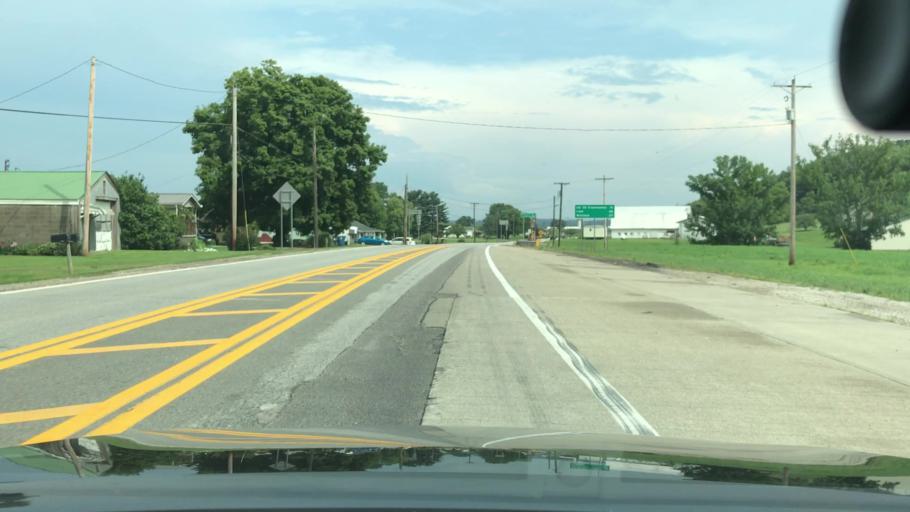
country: US
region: West Virginia
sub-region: Putnam County
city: Buffalo
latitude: 38.7656
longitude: -82.0040
